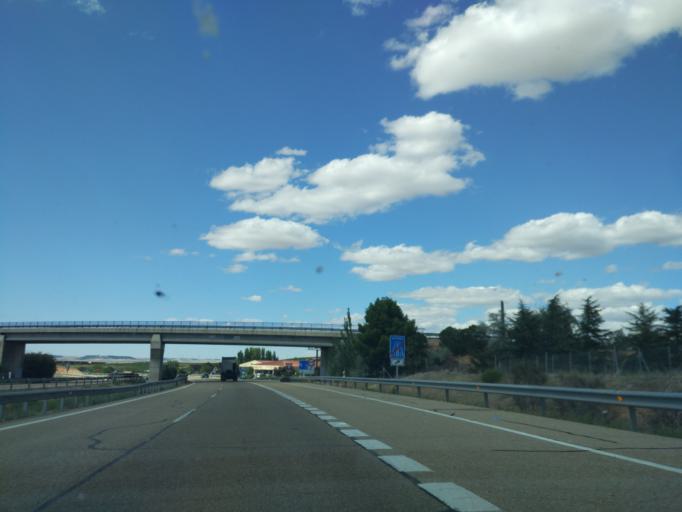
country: ES
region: Castille and Leon
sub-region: Provincia de Valladolid
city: Rueda
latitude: 41.4207
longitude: -4.9651
